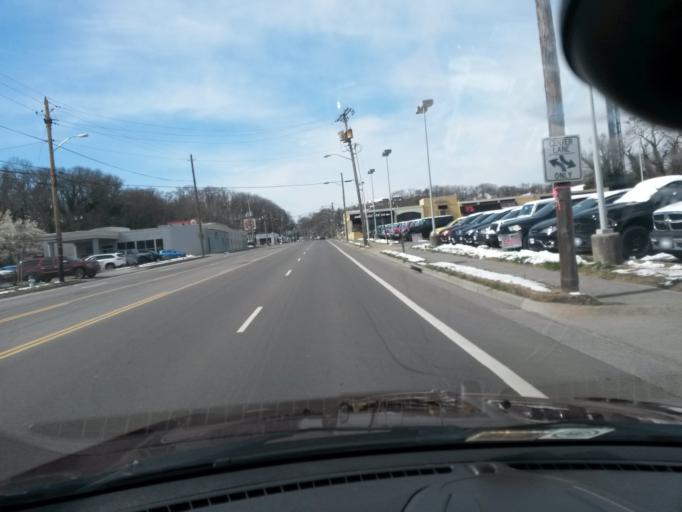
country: US
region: Virginia
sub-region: City of Roanoke
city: Cedar Bluff
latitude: 37.2487
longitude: -79.9572
